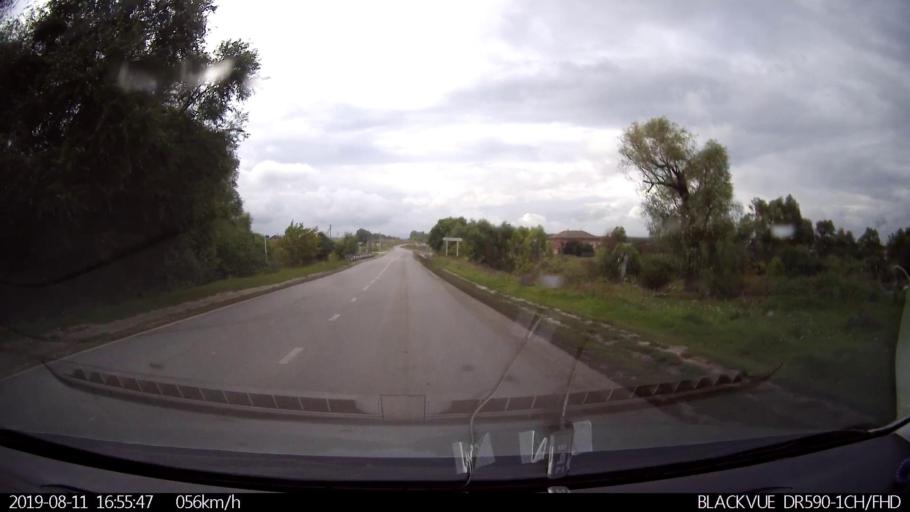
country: RU
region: Ulyanovsk
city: Mayna
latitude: 54.2839
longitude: 47.6602
